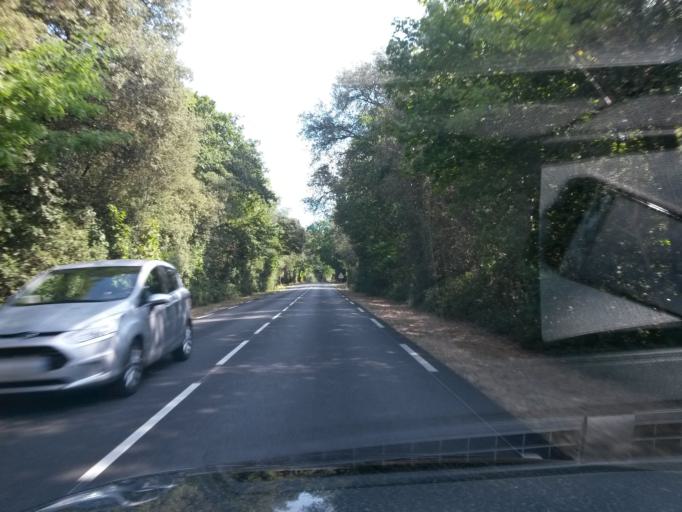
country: FR
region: Pays de la Loire
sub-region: Departement de la Vendee
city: Olonne-sur-Mer
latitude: 46.5708
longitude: -1.8220
